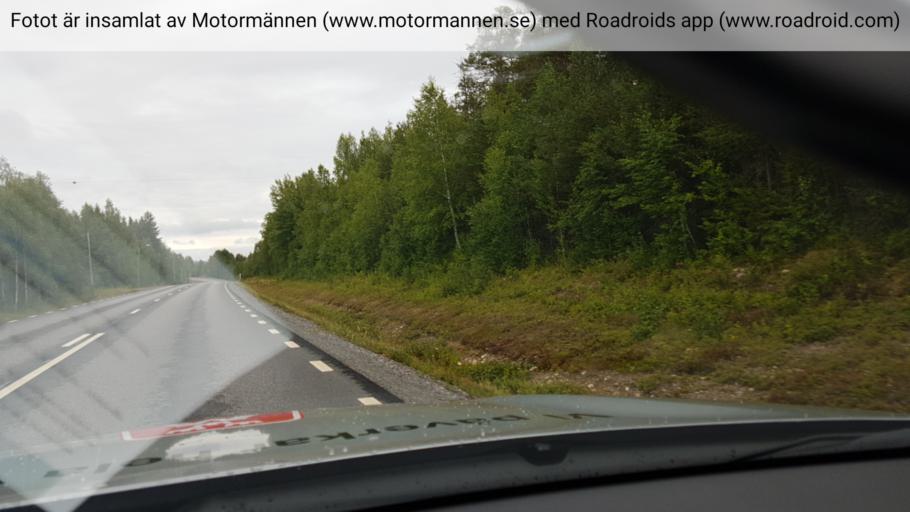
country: SE
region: Norrbotten
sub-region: Alvsbyns Kommun
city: AElvsbyn
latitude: 66.2788
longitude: 20.8206
